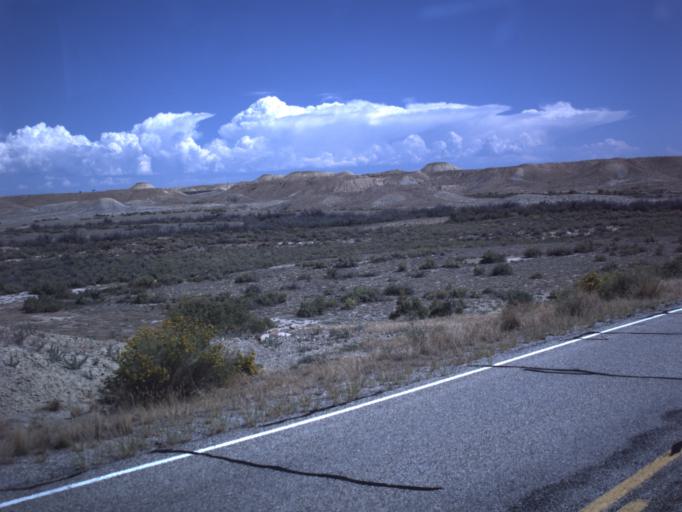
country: US
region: Utah
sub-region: Grand County
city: Moab
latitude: 38.9370
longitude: -109.4018
